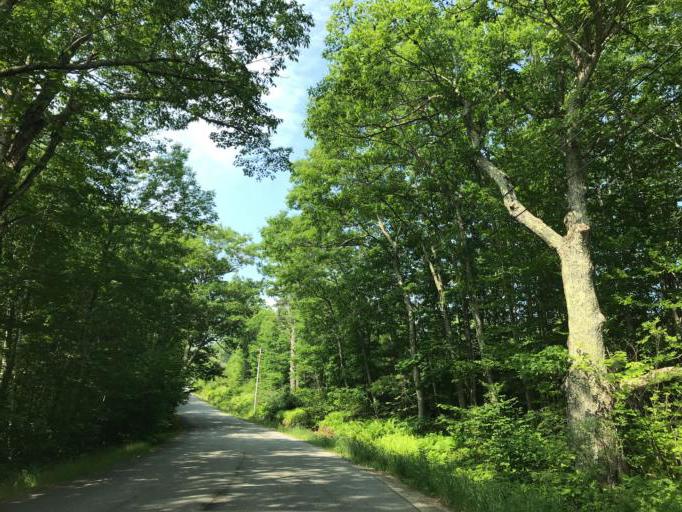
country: US
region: Maine
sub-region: Knox County
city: Hope
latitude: 44.2315
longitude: -69.1514
